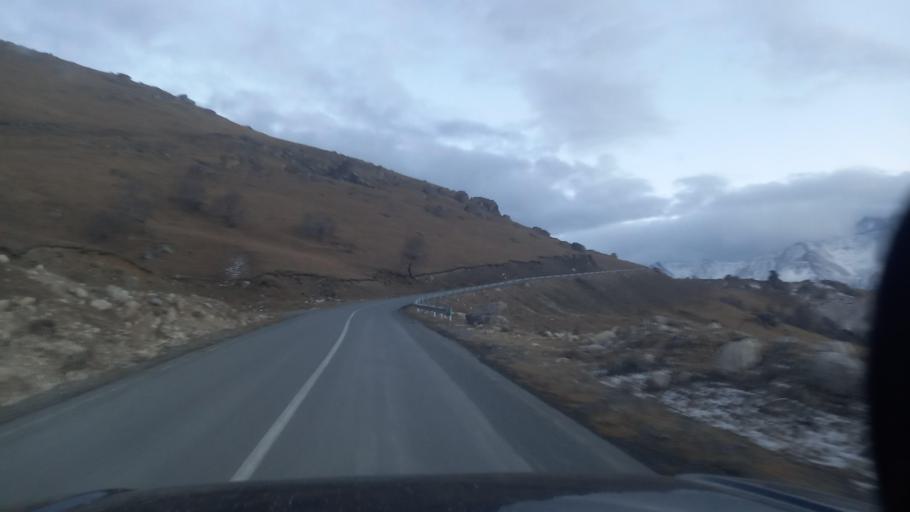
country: RU
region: Ingushetiya
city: Dzhayrakh
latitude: 42.8242
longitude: 44.8268
